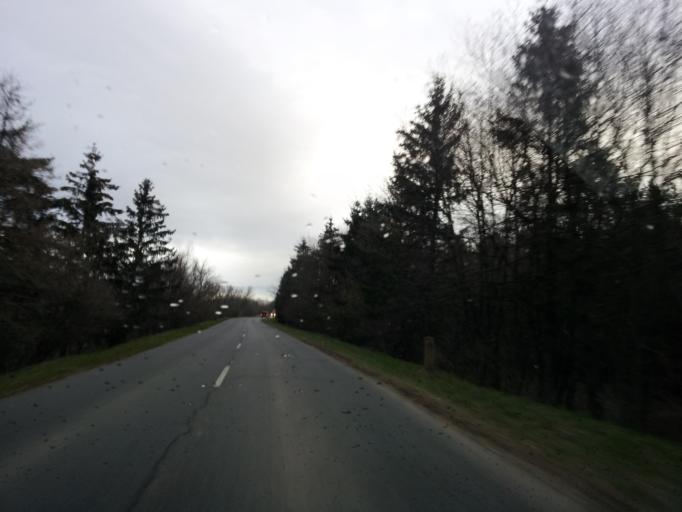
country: HU
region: Vas
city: Koszeg
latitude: 47.3864
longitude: 16.5616
